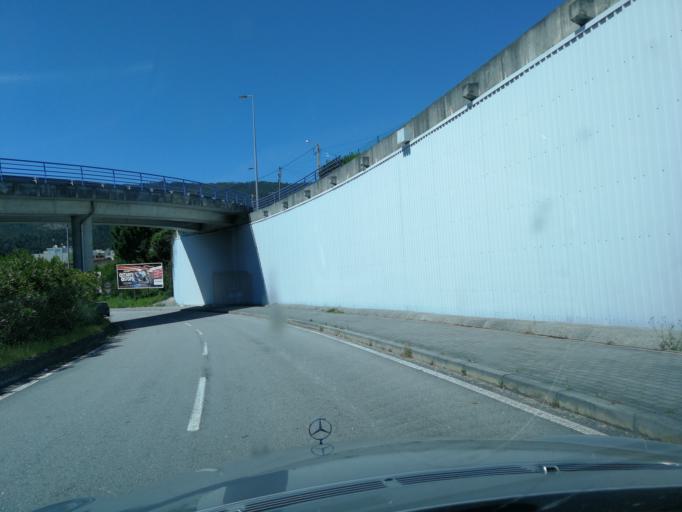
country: PT
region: Viana do Castelo
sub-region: Viana do Castelo
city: Meadela
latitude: 41.7111
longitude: -8.8090
